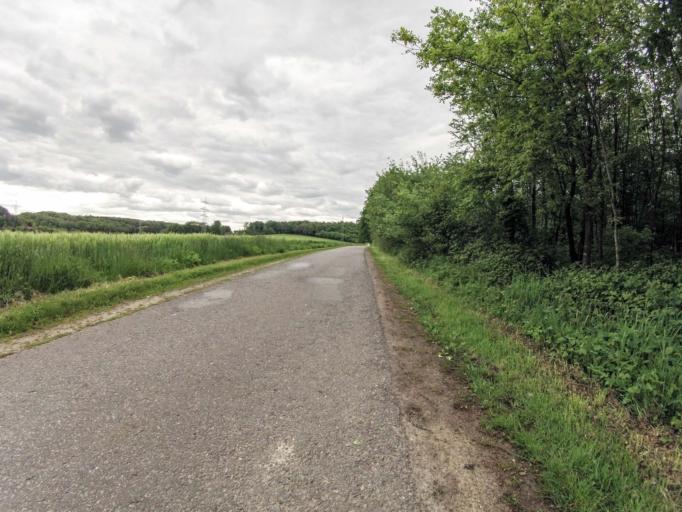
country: DE
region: Lower Saxony
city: Laar
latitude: 52.3251
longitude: 8.2817
